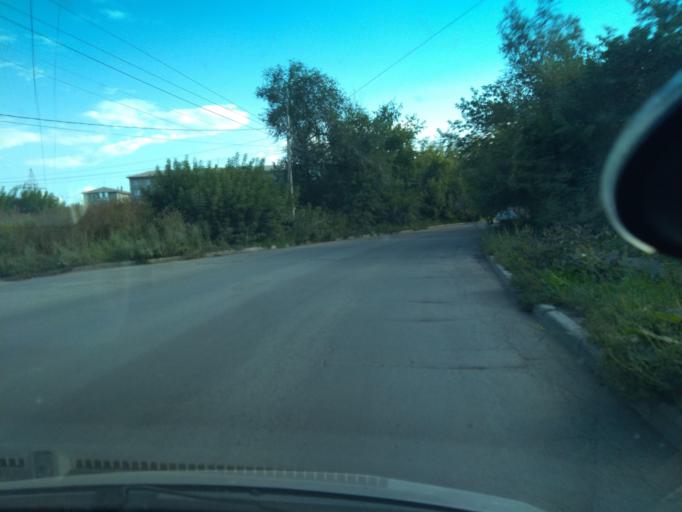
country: RU
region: Krasnoyarskiy
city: Krasnoyarsk
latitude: 55.9753
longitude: 92.9363
